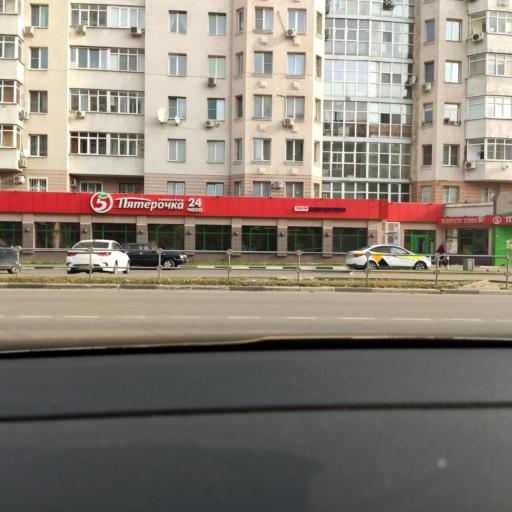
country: RU
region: Moskovskaya
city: Ivanteyevka
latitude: 55.9674
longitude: 37.9130
